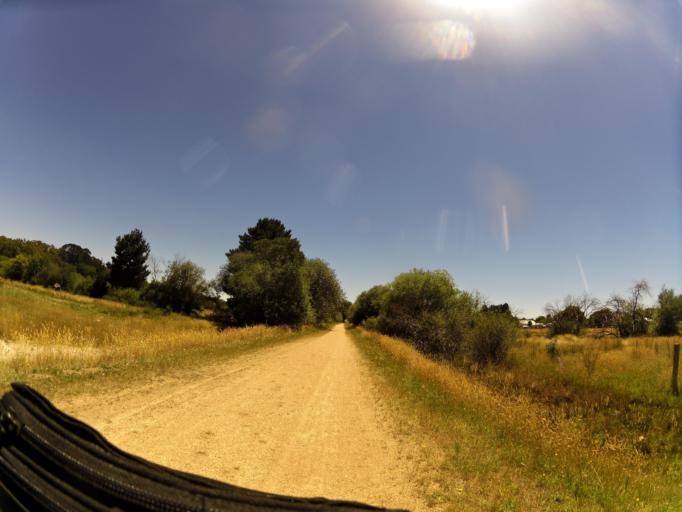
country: AU
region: Victoria
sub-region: Ballarat North
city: Delacombe
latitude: -37.6485
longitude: 143.6800
